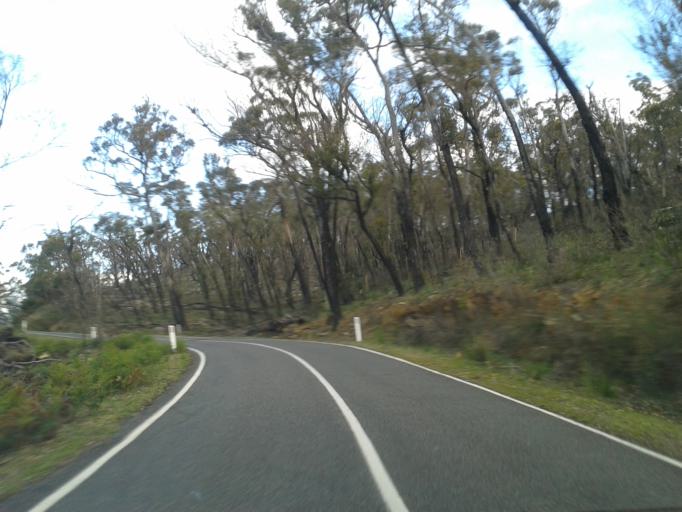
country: AU
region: Victoria
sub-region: Northern Grampians
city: Stawell
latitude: -37.1317
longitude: 142.4276
